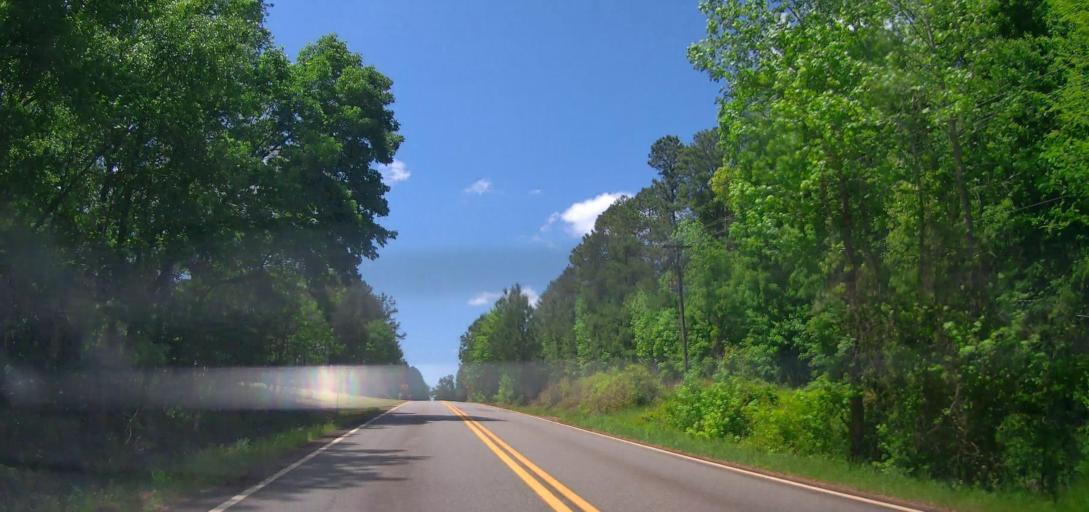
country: US
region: Georgia
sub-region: Jasper County
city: Monticello
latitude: 33.2718
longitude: -83.6712
